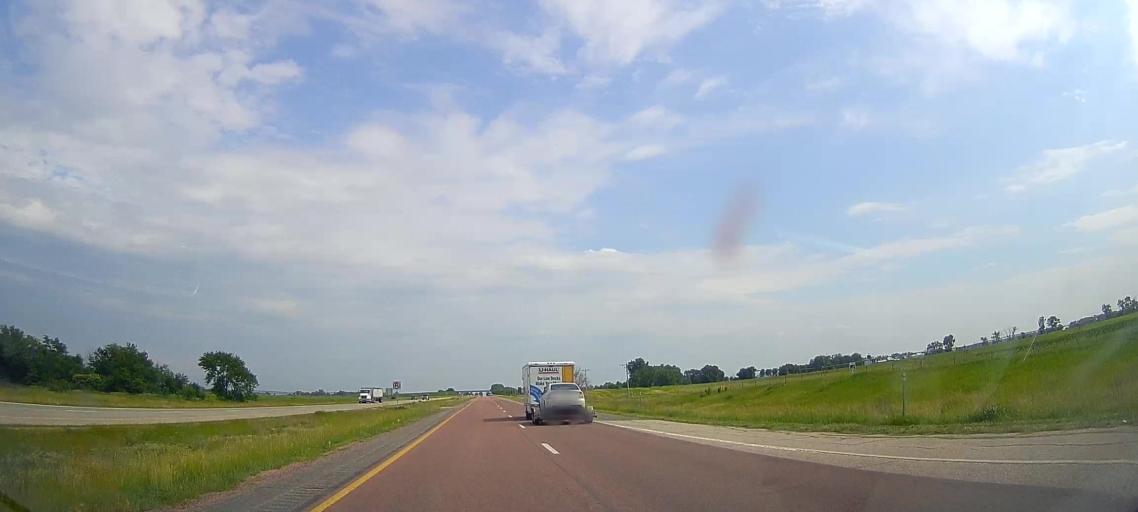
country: US
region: Iowa
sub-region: Monona County
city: Onawa
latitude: 41.9879
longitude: -96.1082
